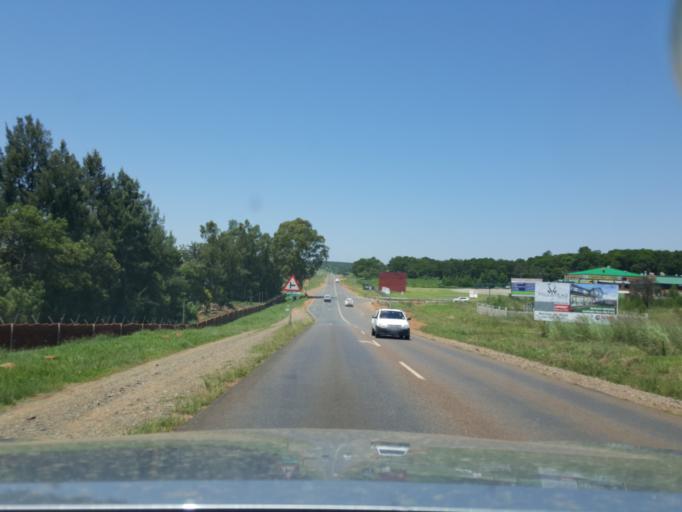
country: ZA
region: Gauteng
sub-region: City of Tshwane Metropolitan Municipality
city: Centurion
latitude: -25.8482
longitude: 28.3299
